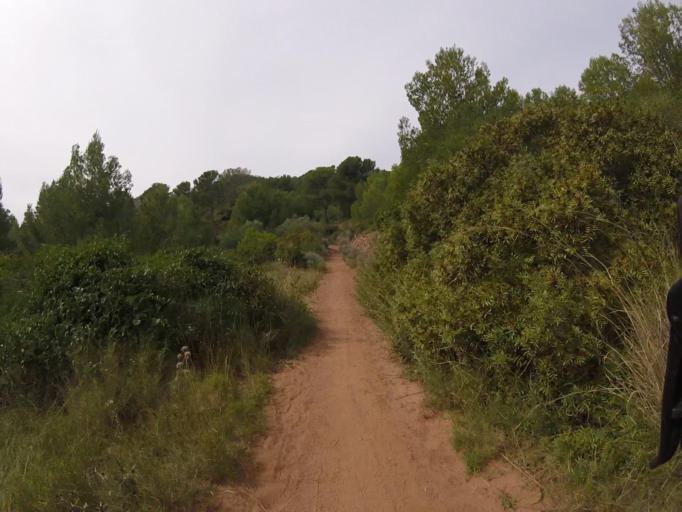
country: ES
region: Valencia
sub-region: Provincia de Castello
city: Benicassim
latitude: 40.0727
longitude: 0.0353
